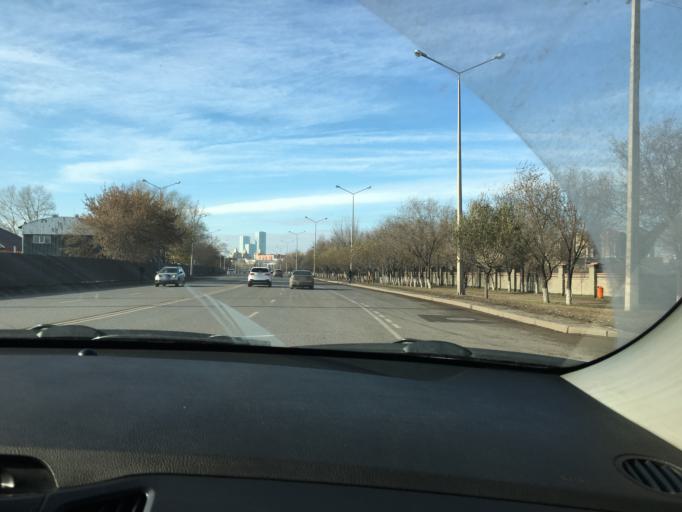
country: KZ
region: Astana Qalasy
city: Astana
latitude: 51.1569
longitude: 71.4507
